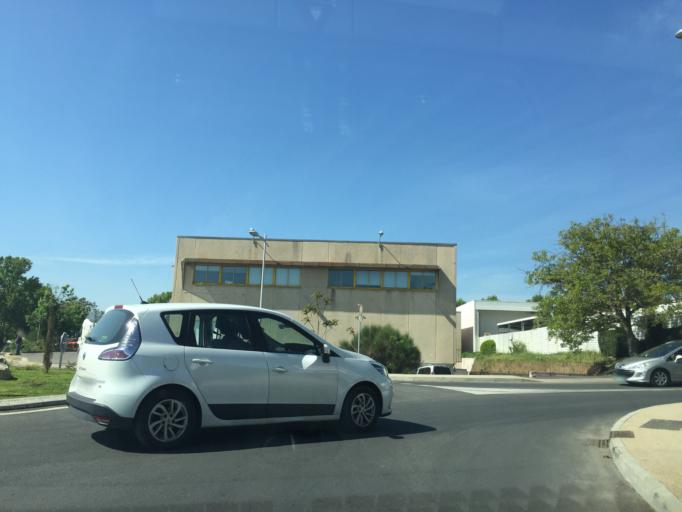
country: FR
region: Provence-Alpes-Cote d'Azur
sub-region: Departement des Alpes-de-Haute-Provence
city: Manosque
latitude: 43.8185
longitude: 5.7999
